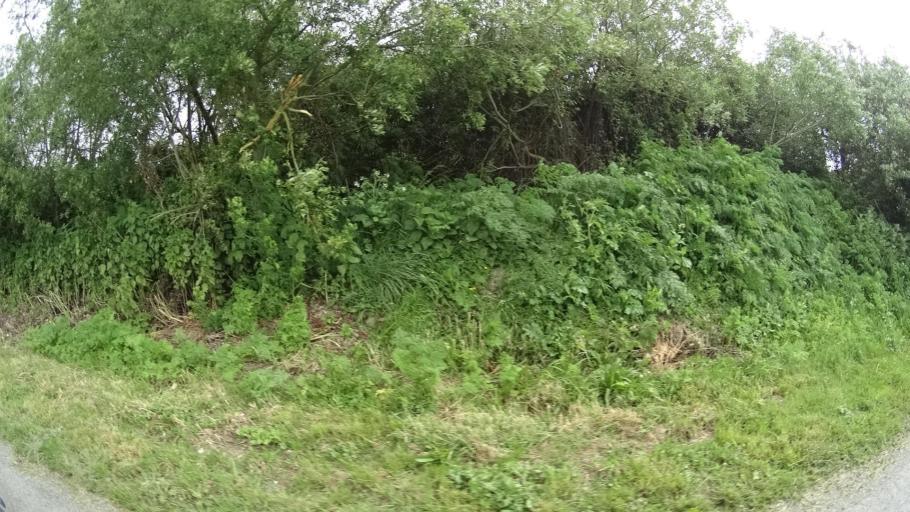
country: US
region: California
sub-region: Humboldt County
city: Fortuna
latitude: 40.5899
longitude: -124.1881
